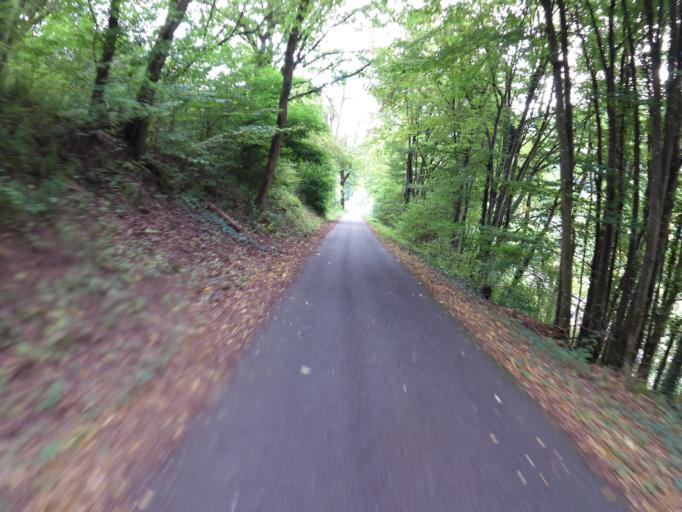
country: DE
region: Rheinland-Pfalz
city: Gondorf
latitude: 49.9578
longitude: 6.5981
